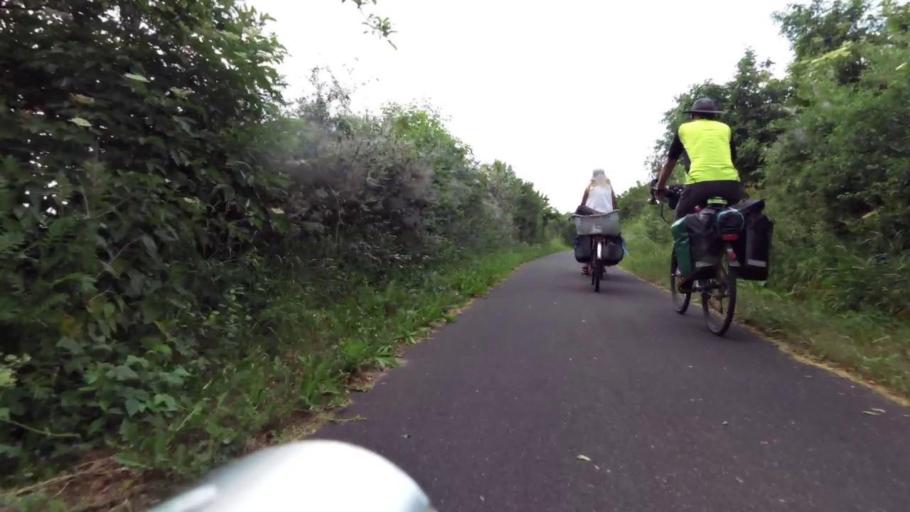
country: PL
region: Kujawsko-Pomorskie
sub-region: Powiat torunski
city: Lubianka
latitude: 53.1178
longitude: 18.4694
